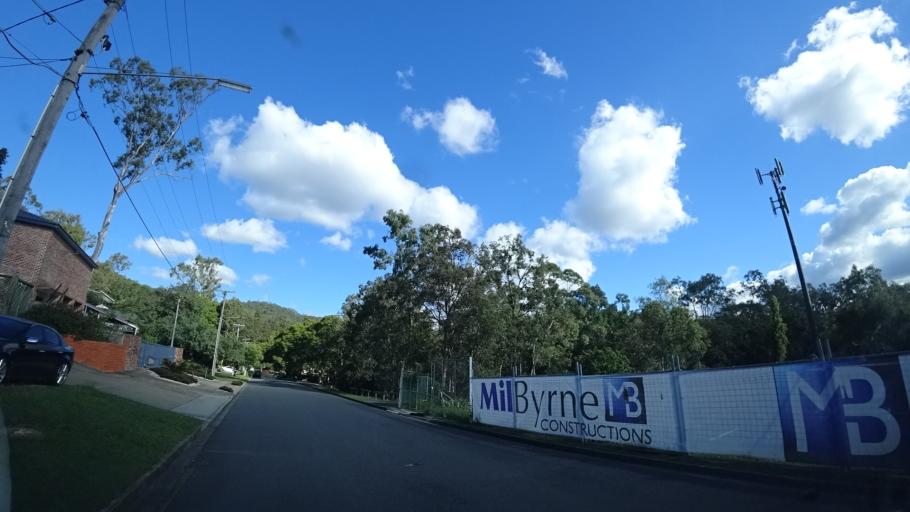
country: AU
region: Queensland
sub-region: Brisbane
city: Toowong
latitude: -27.4475
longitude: 152.9603
